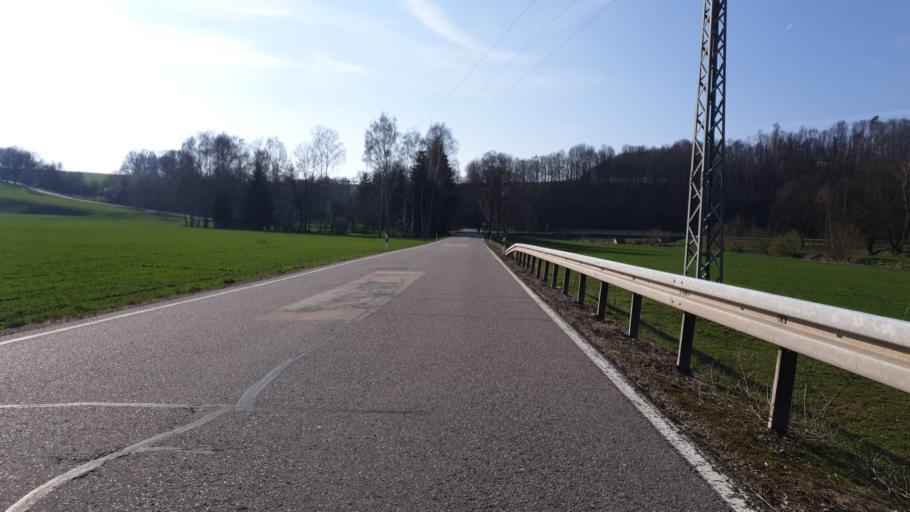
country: DE
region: Saxony
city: Taura
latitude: 50.9371
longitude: 12.8431
